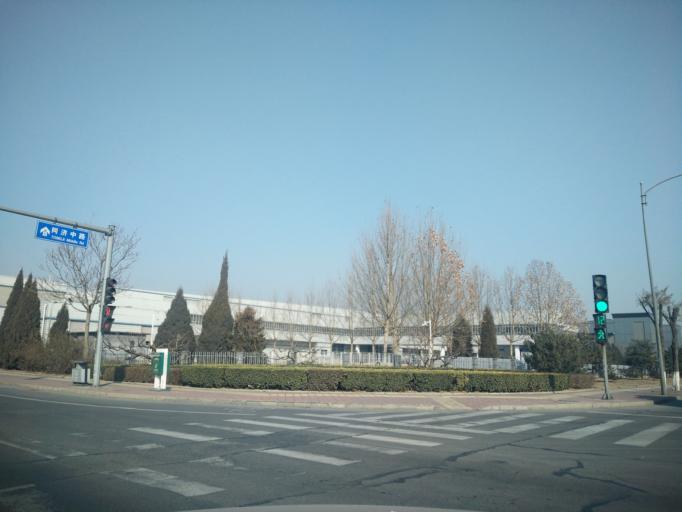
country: CN
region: Beijing
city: Jiugong
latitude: 39.7909
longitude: 116.5198
